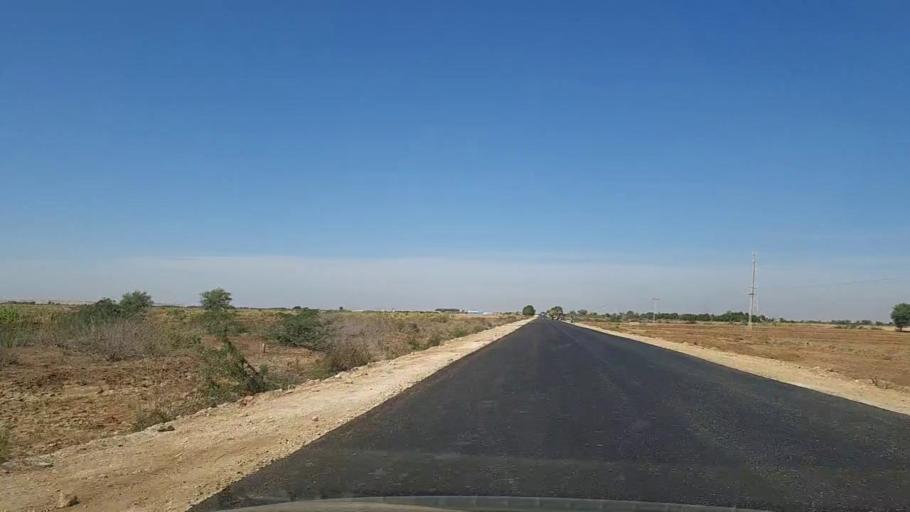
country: PK
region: Sindh
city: Kotri
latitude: 25.2454
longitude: 68.2295
